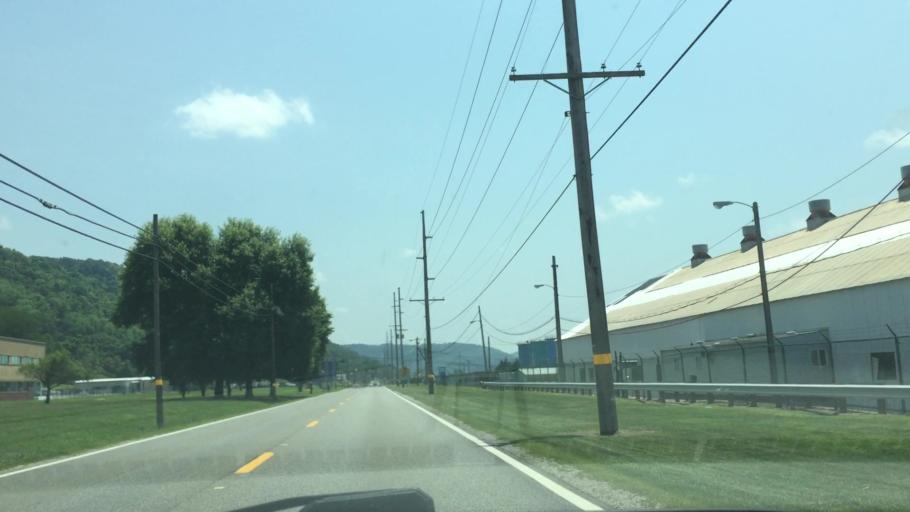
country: US
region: West Virginia
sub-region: Wetzel County
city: New Martinsville
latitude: 39.7498
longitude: -80.8514
